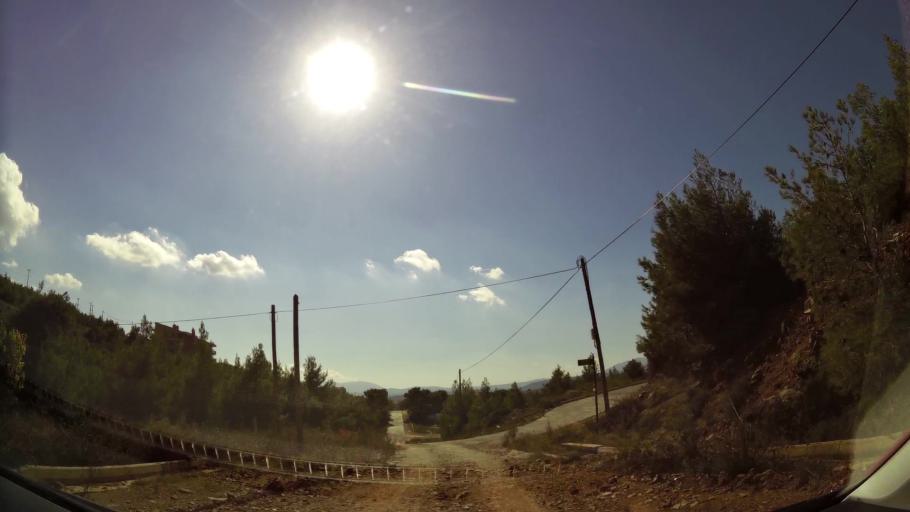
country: GR
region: Attica
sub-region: Nomarchia Anatolikis Attikis
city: Dioni
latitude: 38.0320
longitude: 23.9337
